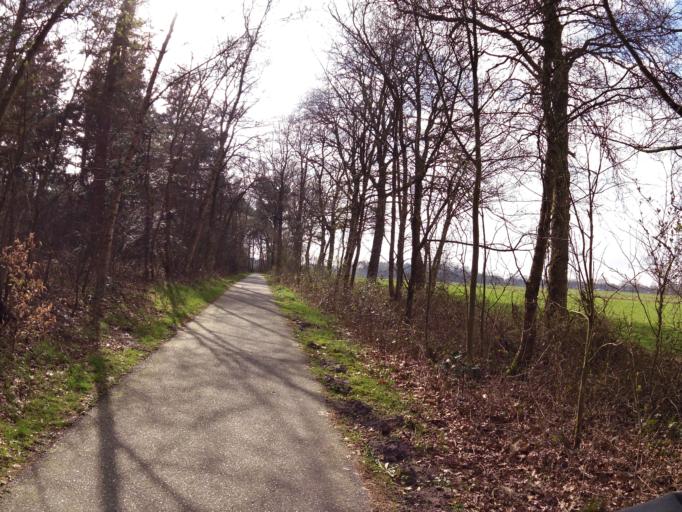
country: NL
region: Friesland
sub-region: Gemeente Weststellingwerf
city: Noordwolde
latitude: 52.8782
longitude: 6.2123
